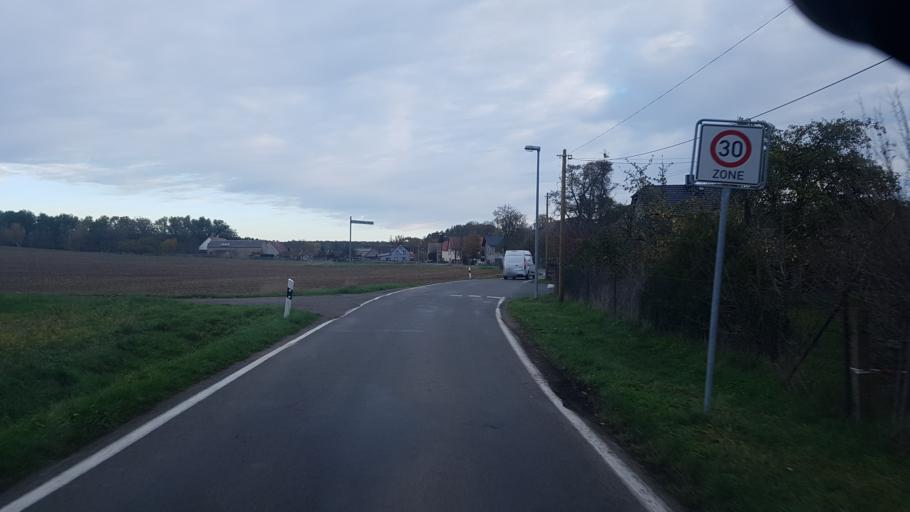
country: DE
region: Saxony
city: Dahlen
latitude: 51.3845
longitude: 13.0375
